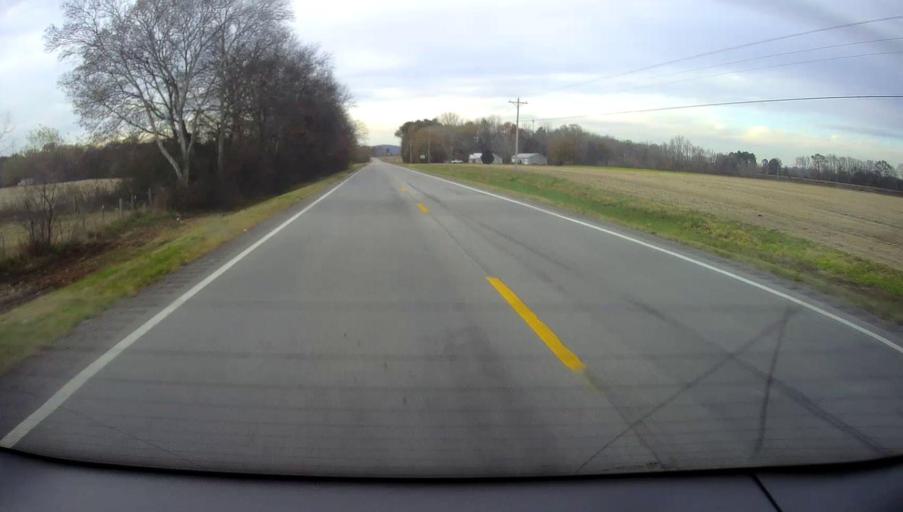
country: US
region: Alabama
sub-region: Marshall County
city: Arab
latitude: 34.4080
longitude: -86.6931
